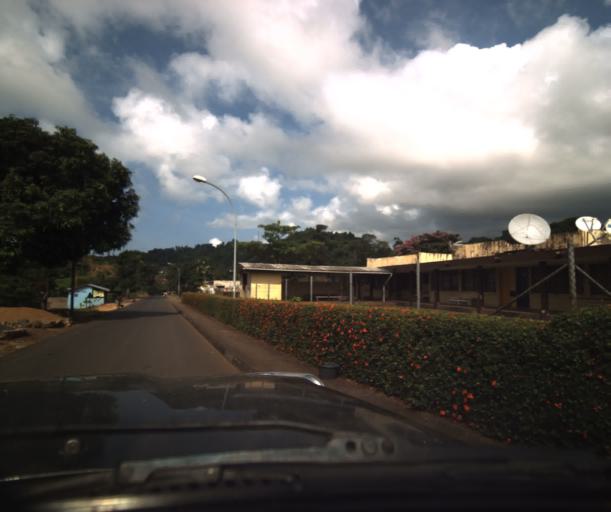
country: CM
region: South-West Province
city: Limbe
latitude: 4.0191
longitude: 9.1871
